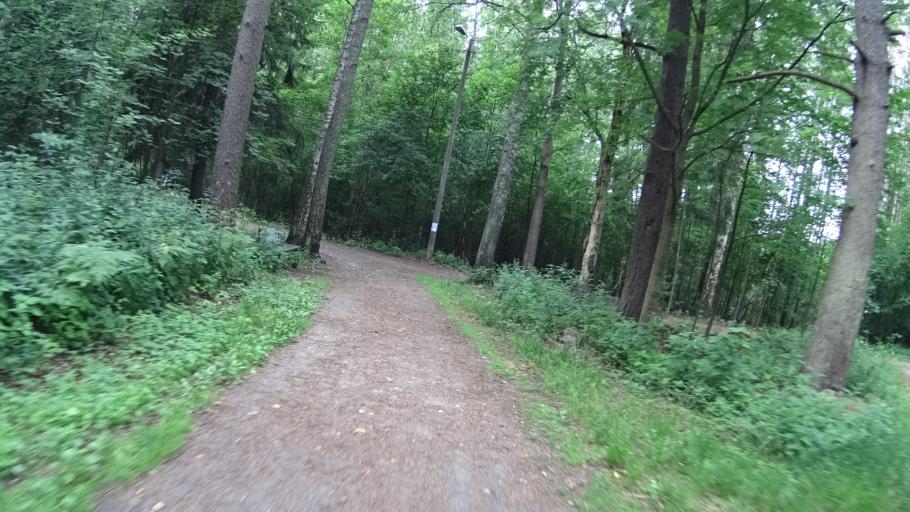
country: FI
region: Uusimaa
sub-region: Helsinki
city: Teekkarikylae
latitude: 60.2203
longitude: 24.8540
